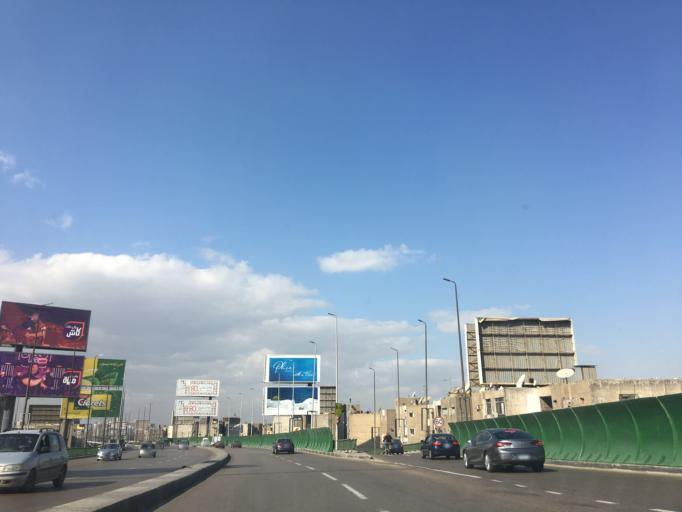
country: EG
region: Muhafazat al Qahirah
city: Cairo
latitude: 30.0611
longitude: 31.3013
